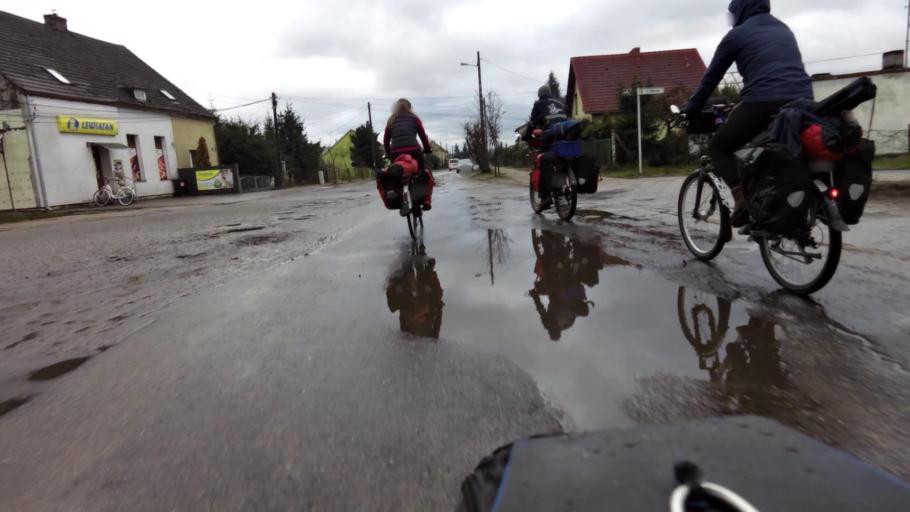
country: PL
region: Lubusz
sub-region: Powiat gorzowski
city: Witnica
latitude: 52.6822
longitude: 14.8899
